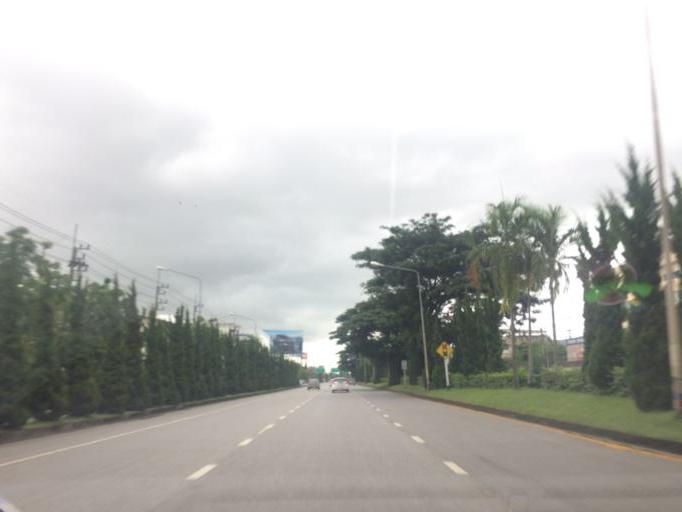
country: TH
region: Chiang Rai
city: Chiang Rai
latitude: 19.8935
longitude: 99.8374
